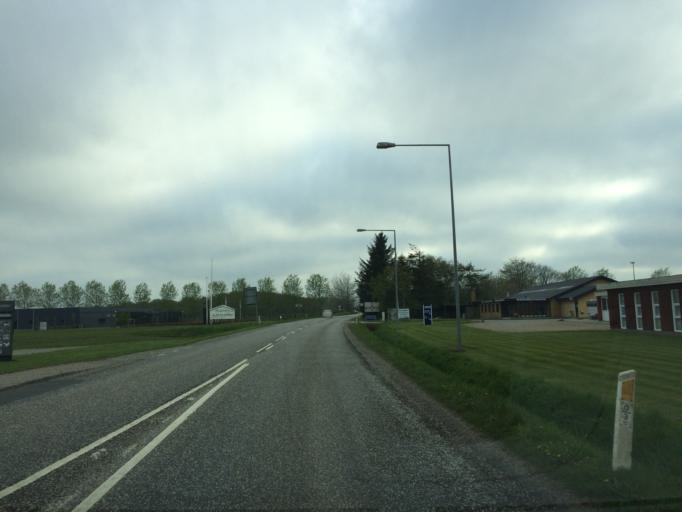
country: DK
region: Central Jutland
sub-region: Herning Kommune
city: Avlum
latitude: 56.2581
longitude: 8.7904
